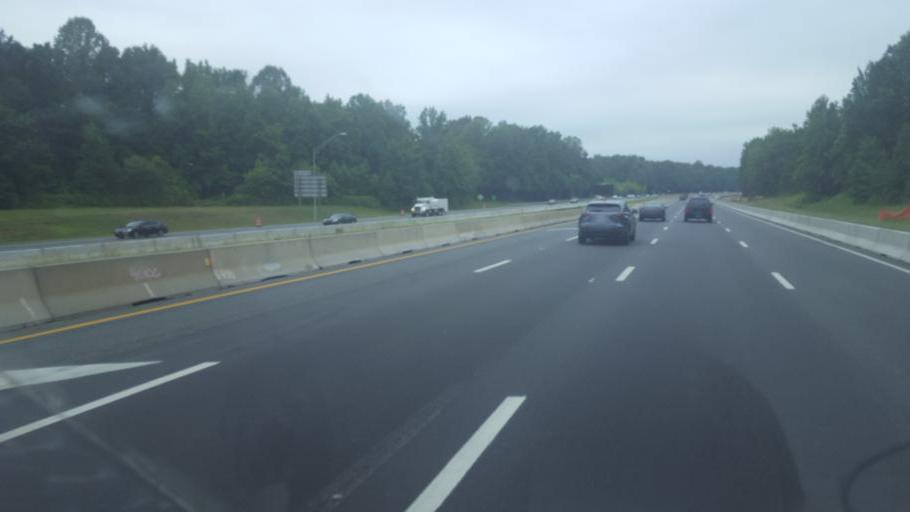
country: US
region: North Carolina
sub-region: Mecklenburg County
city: Charlotte
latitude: 35.2848
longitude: -80.8486
